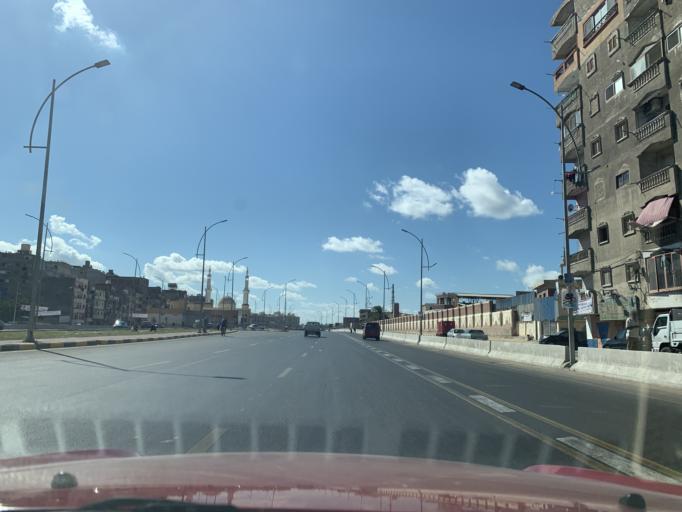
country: EG
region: Alexandria
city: Alexandria
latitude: 31.2225
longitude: 29.9697
